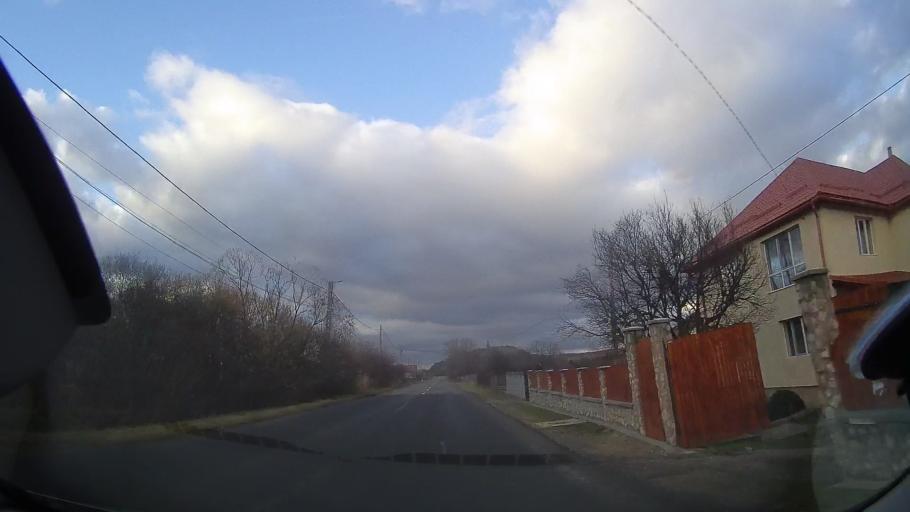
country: RO
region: Cluj
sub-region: Comuna Calatele
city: Calatele
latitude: 46.7772
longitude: 23.0065
